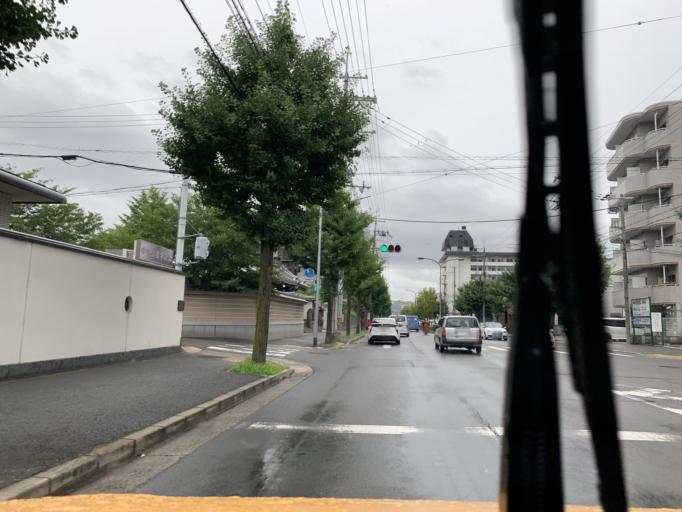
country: JP
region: Kyoto
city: Kyoto
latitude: 35.0109
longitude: 135.7212
